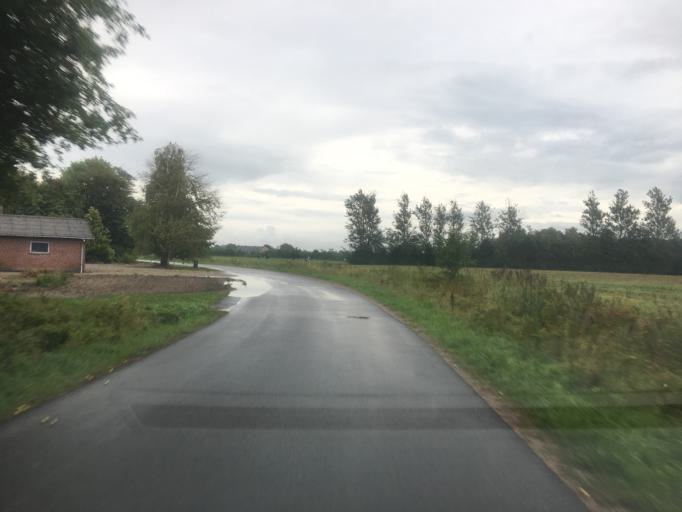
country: DK
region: South Denmark
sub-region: Tonder Kommune
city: Logumkloster
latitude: 54.9911
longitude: 8.9839
